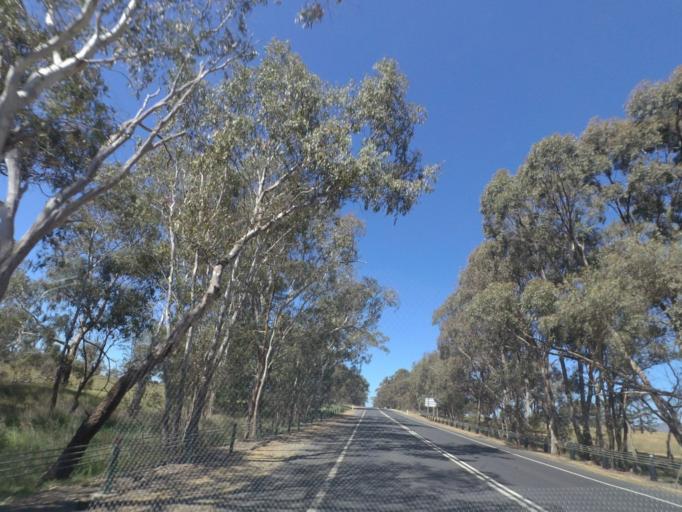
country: AU
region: Victoria
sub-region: Murrindindi
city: Kinglake West
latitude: -37.0294
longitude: 145.0739
